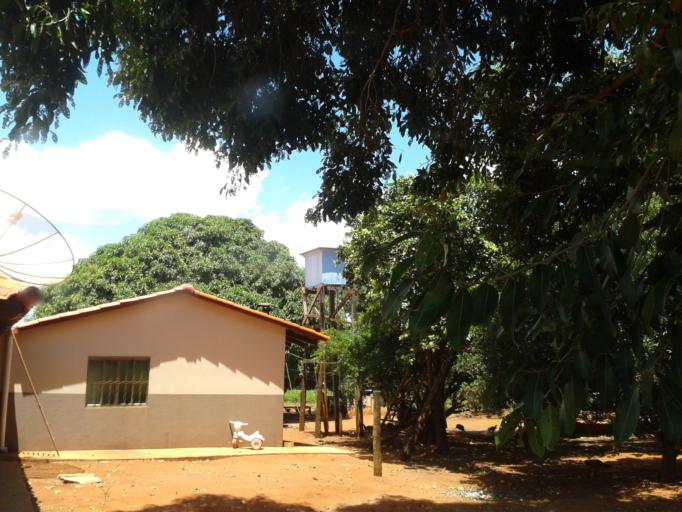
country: BR
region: Minas Gerais
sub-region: Centralina
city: Centralina
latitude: -18.6910
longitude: -49.1608
